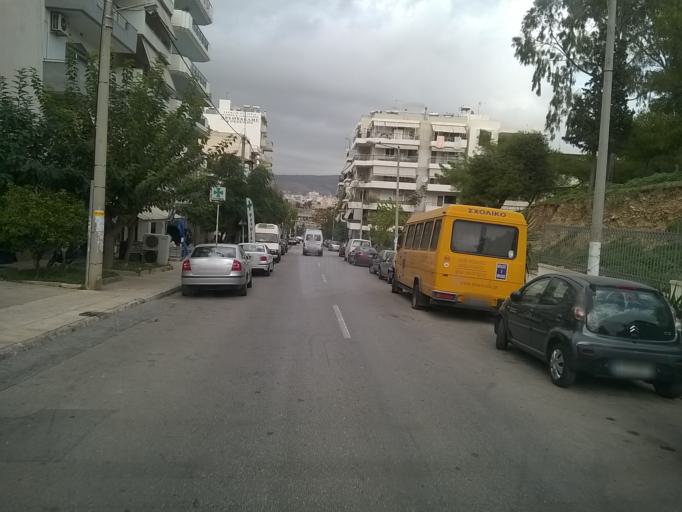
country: GR
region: Attica
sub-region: Nomos Attikis
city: Piraeus
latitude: 37.9364
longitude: 23.6306
